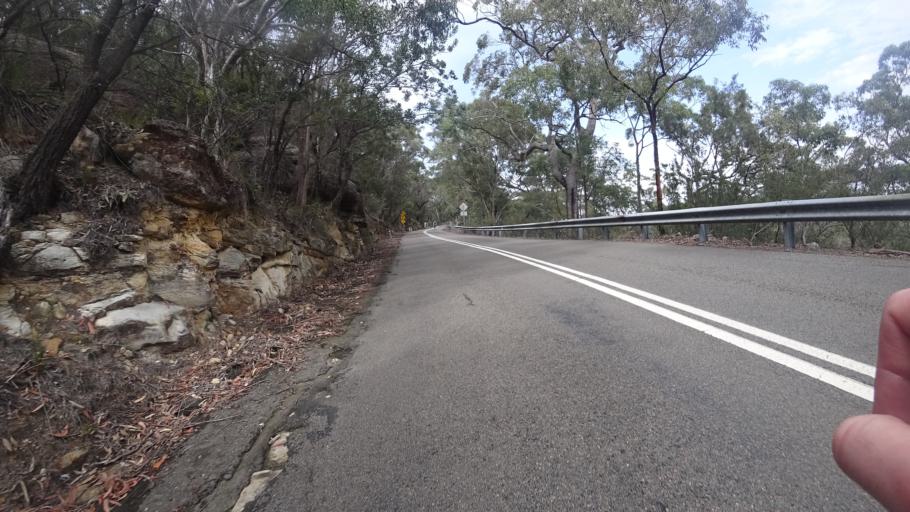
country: AU
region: New South Wales
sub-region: Hornsby Shire
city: Berowra
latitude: -33.6580
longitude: 151.1496
